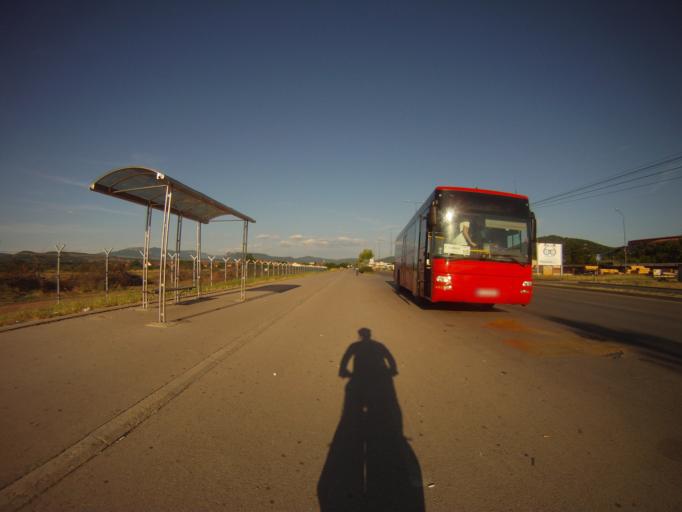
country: RS
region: Central Serbia
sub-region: Nisavski Okrug
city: Nis
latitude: 43.3077
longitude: 21.9518
